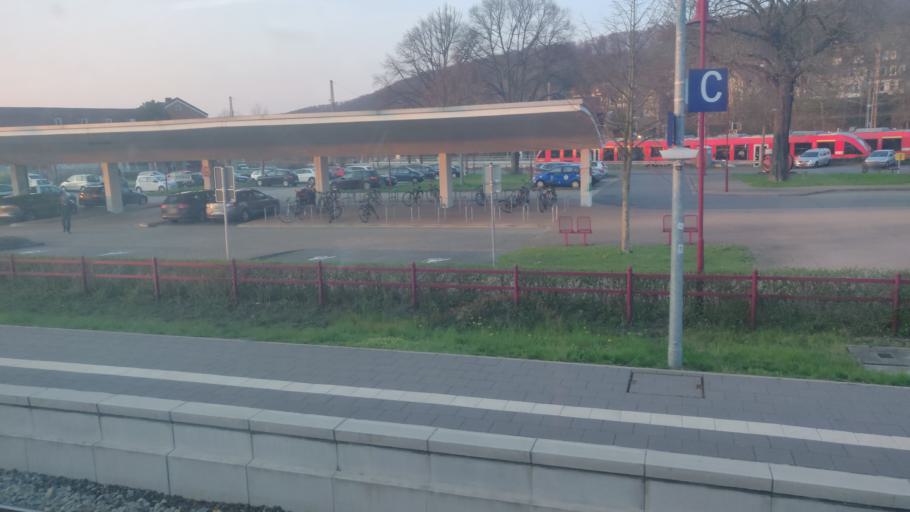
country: DE
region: Lower Saxony
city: Kreiensen
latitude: 51.8517
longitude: 9.9663
